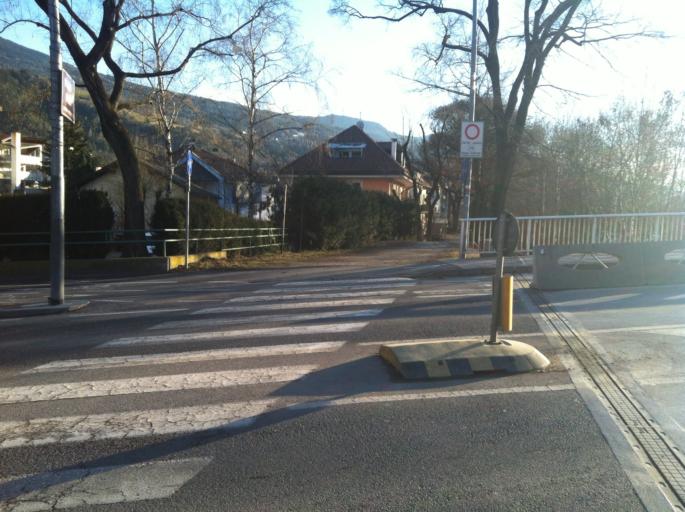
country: IT
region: Trentino-Alto Adige
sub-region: Bolzano
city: Bressanone
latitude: 46.7107
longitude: 11.6605
